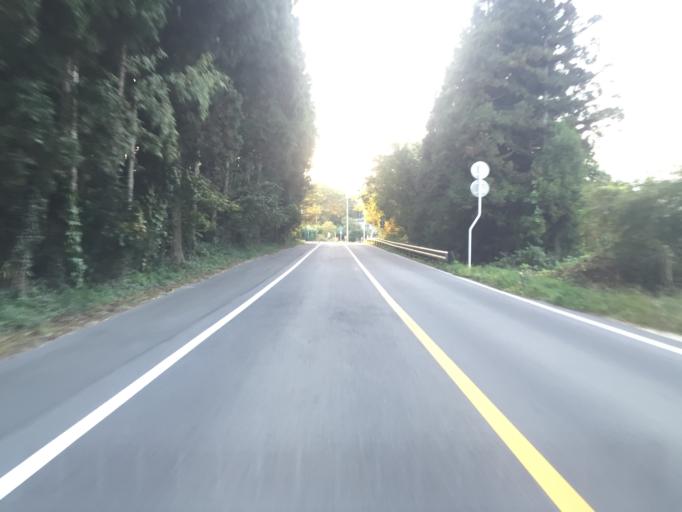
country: JP
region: Fukushima
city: Motomiya
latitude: 37.5536
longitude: 140.3593
